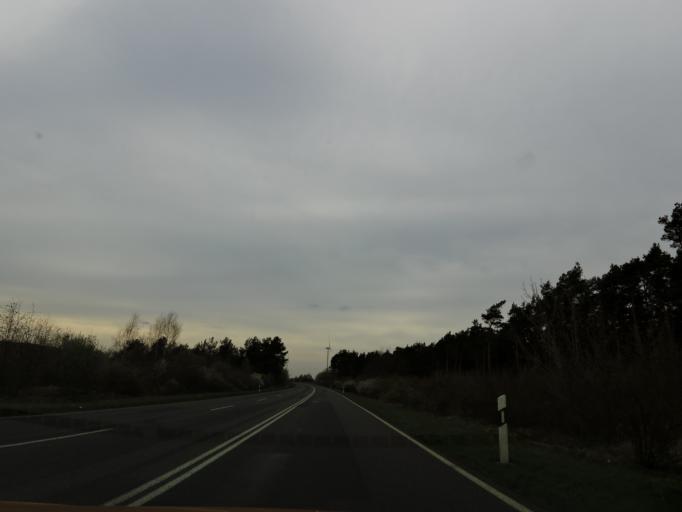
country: DE
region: Brandenburg
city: Beeskow
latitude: 52.1988
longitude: 14.2602
